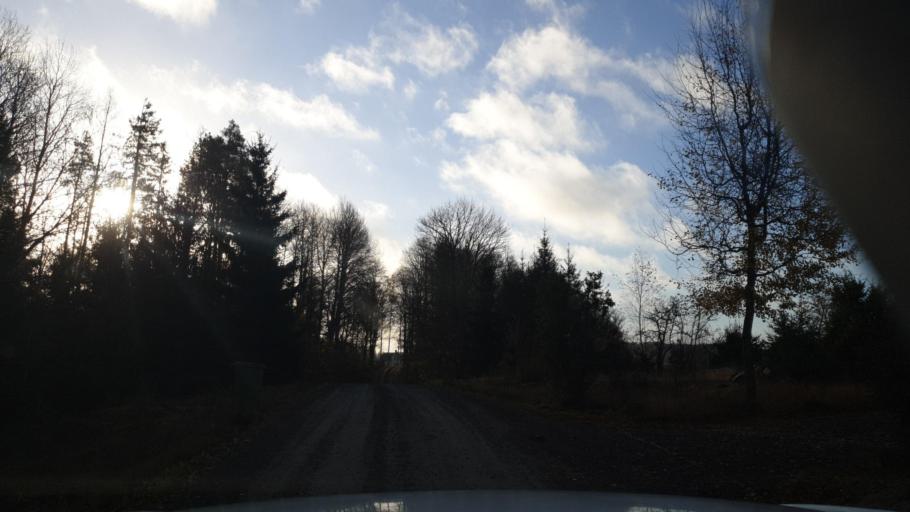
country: SE
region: Vaermland
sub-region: Grums Kommun
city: Grums
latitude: 59.4913
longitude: 12.9281
